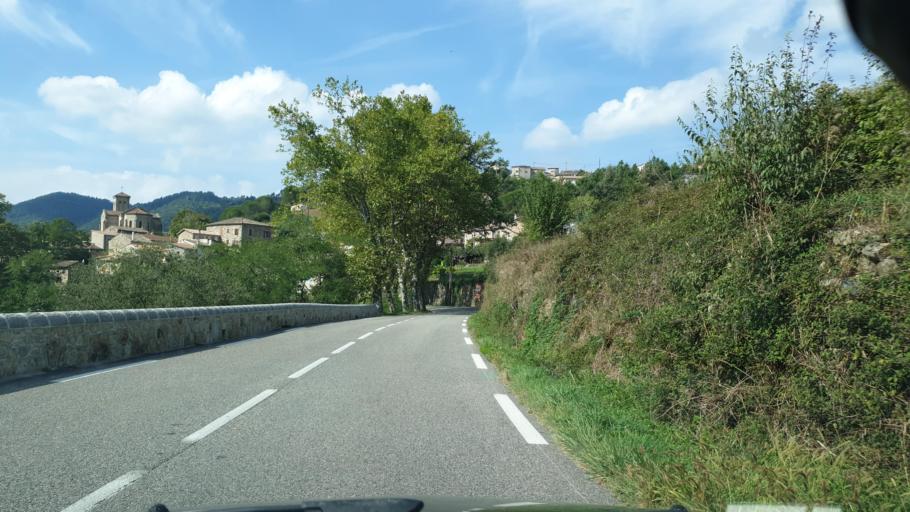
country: FR
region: Rhone-Alpes
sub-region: Departement de l'Ardeche
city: Saint-Sauveur-de-Montagut
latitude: 44.8071
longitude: 4.6278
